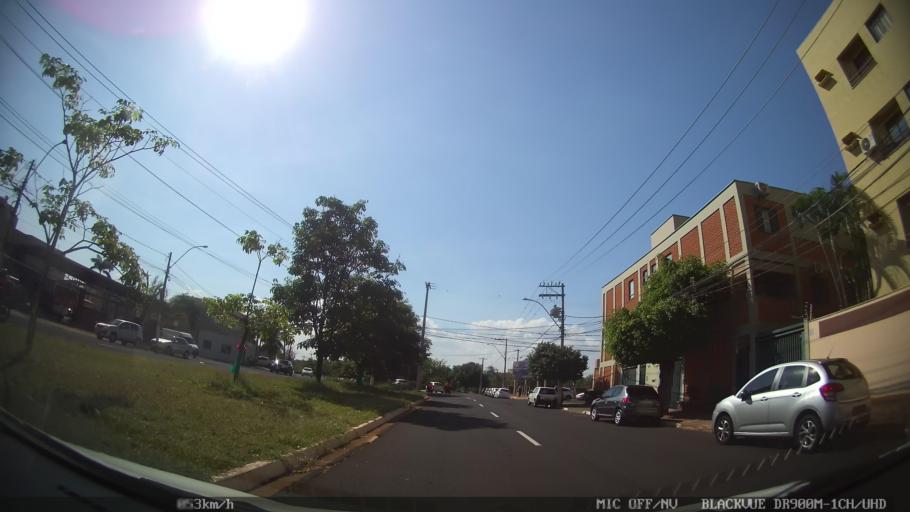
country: BR
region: Sao Paulo
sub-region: Ribeirao Preto
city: Ribeirao Preto
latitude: -21.2103
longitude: -47.8165
